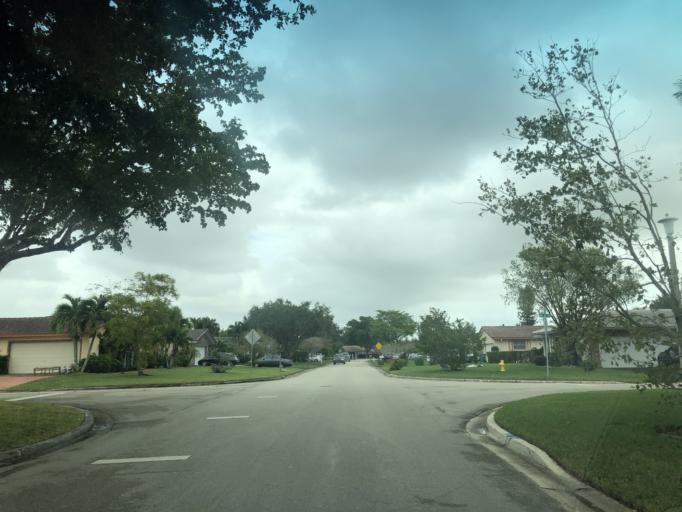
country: US
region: Florida
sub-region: Broward County
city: Coral Springs
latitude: 26.2548
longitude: -80.2406
